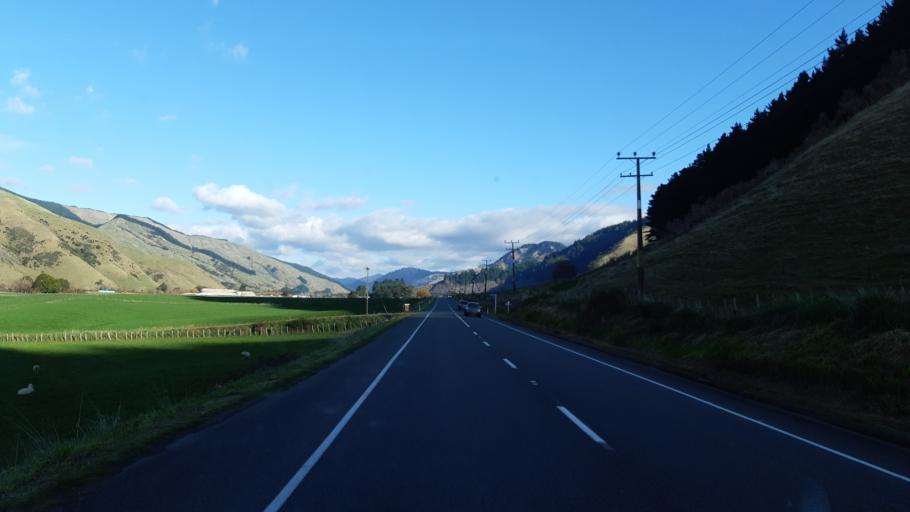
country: NZ
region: Marlborough
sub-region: Marlborough District
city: Picton
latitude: -41.3086
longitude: 173.7672
